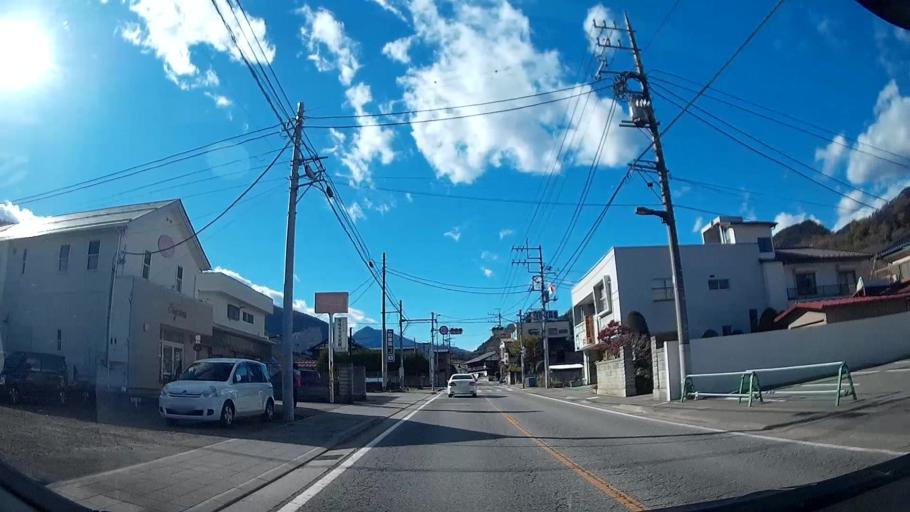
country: JP
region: Yamanashi
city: Otsuki
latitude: 35.6057
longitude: 138.9300
